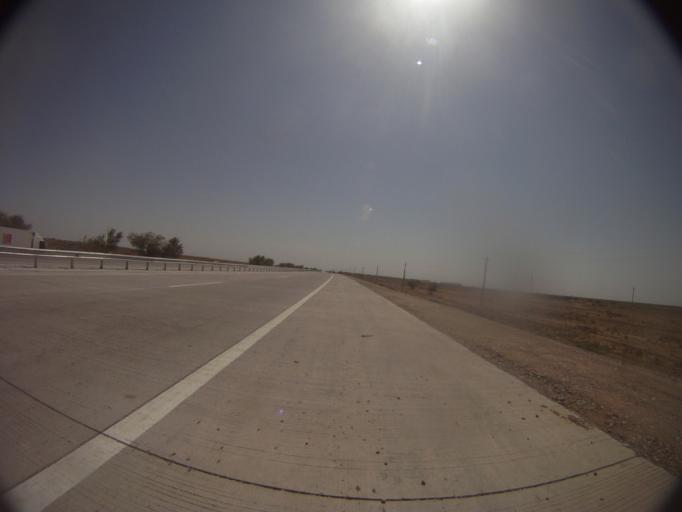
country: KZ
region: Ongtustik Qazaqstan
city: Bayaldyr
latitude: 43.0754
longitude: 68.6584
